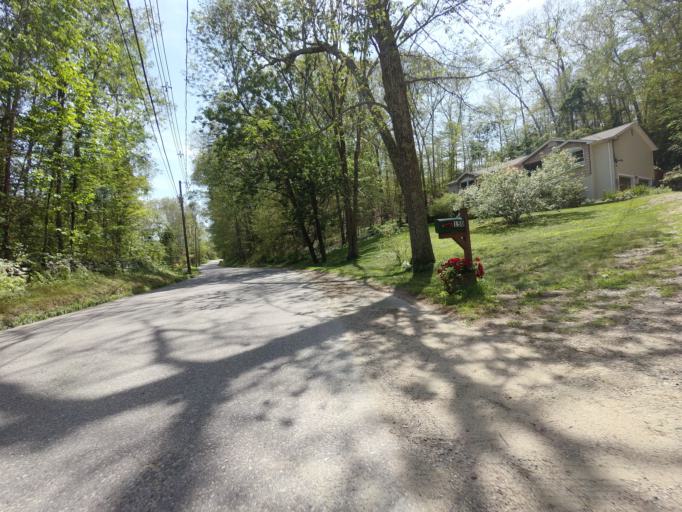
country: US
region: Connecticut
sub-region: Windham County
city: East Brooklyn
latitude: 41.8372
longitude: -71.9359
